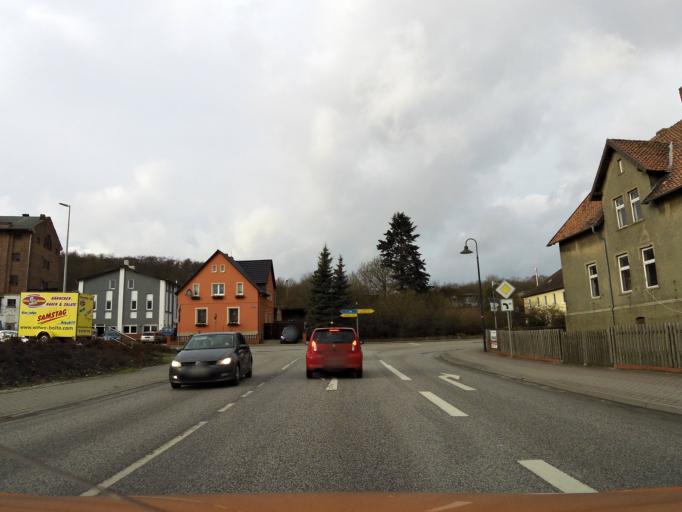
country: DE
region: Saxony-Anhalt
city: Weferlingen
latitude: 52.3108
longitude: 11.0482
